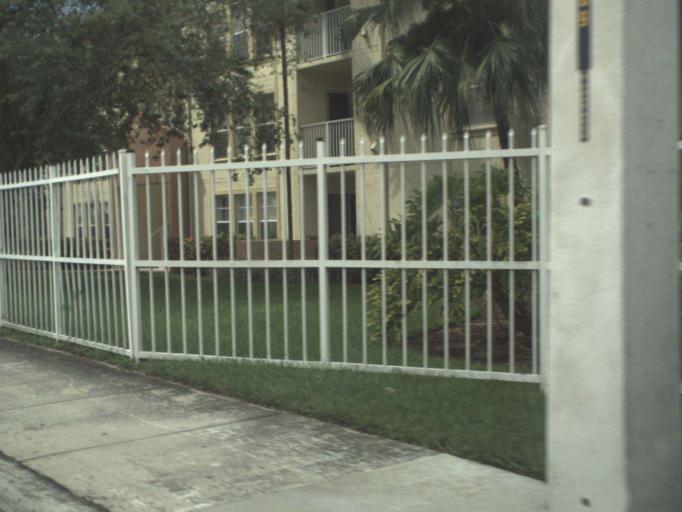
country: US
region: Florida
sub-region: Miami-Dade County
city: The Crossings
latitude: 25.6810
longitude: -80.4168
